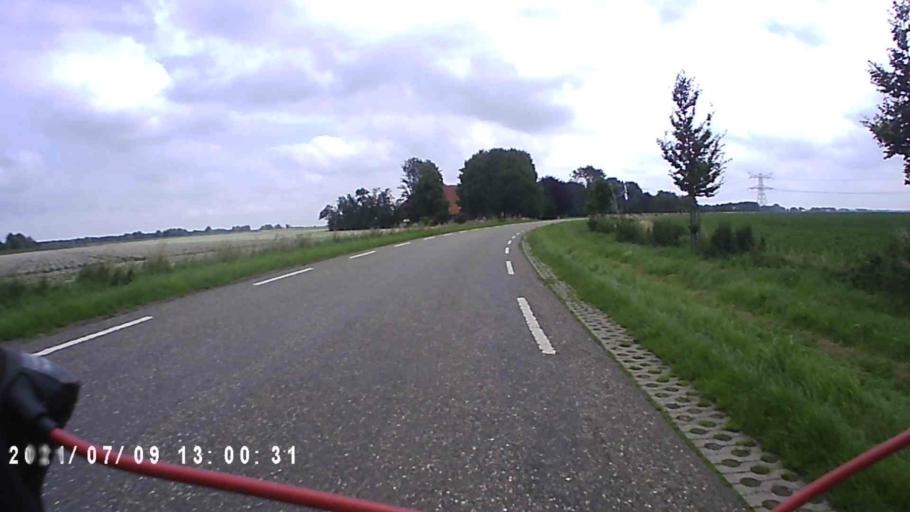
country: NL
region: Groningen
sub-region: Gemeente  Oldambt
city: Winschoten
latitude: 53.1353
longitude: 7.0715
